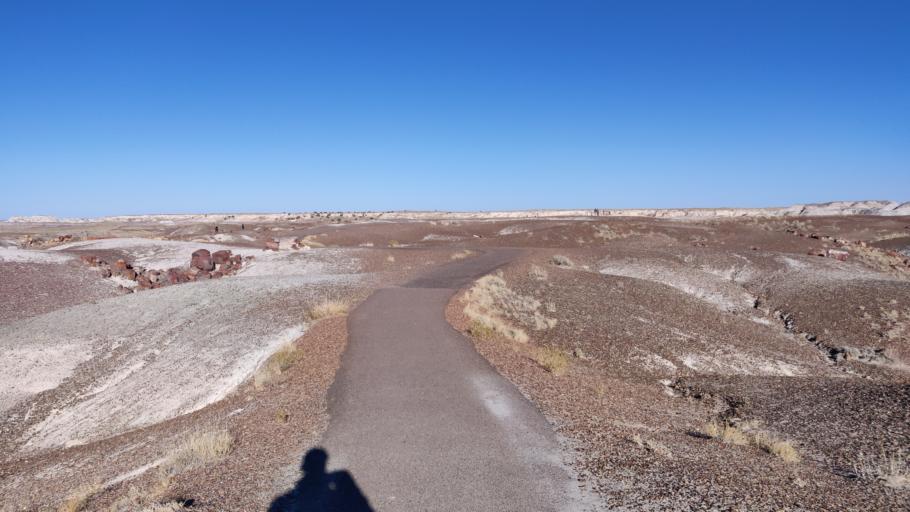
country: US
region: Arizona
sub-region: Navajo County
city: Holbrook
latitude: 34.8642
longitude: -109.7895
